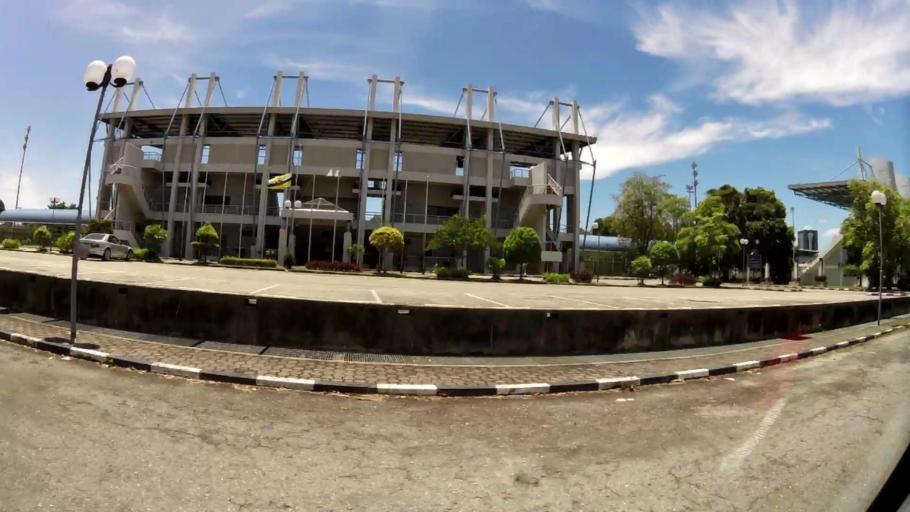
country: BN
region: Brunei and Muara
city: Bandar Seri Begawan
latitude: 4.9312
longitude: 114.9465
